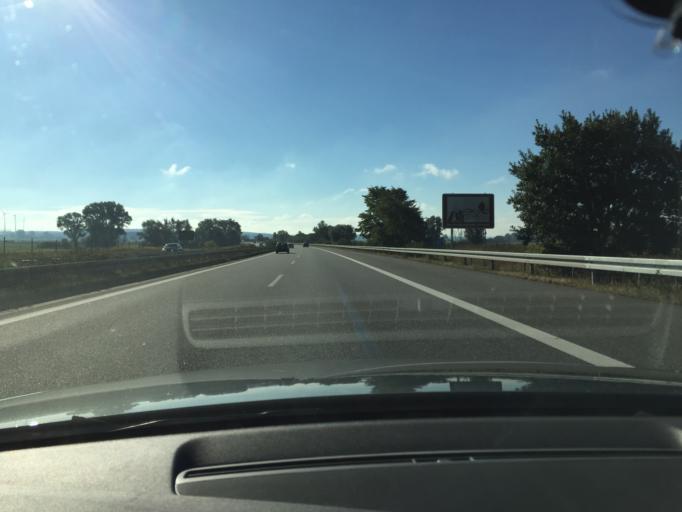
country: DE
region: Mecklenburg-Vorpommern
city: Laage
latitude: 53.8652
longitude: 12.2595
